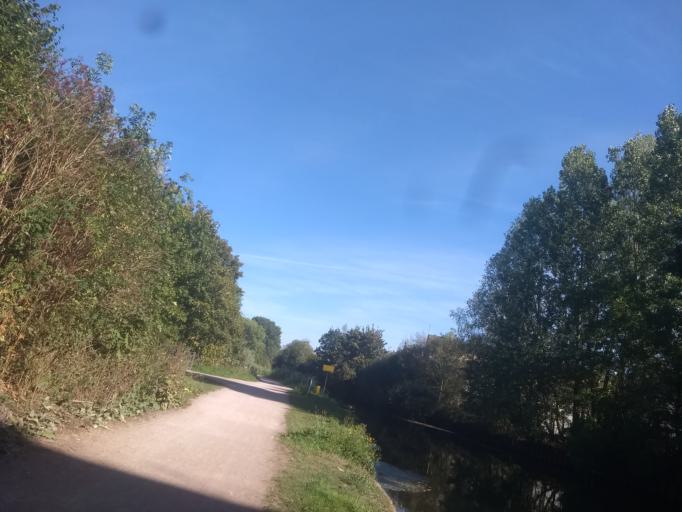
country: FR
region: Nord-Pas-de-Calais
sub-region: Departement du Pas-de-Calais
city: Saint-Laurent-Blangy
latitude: 50.3005
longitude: 2.8227
